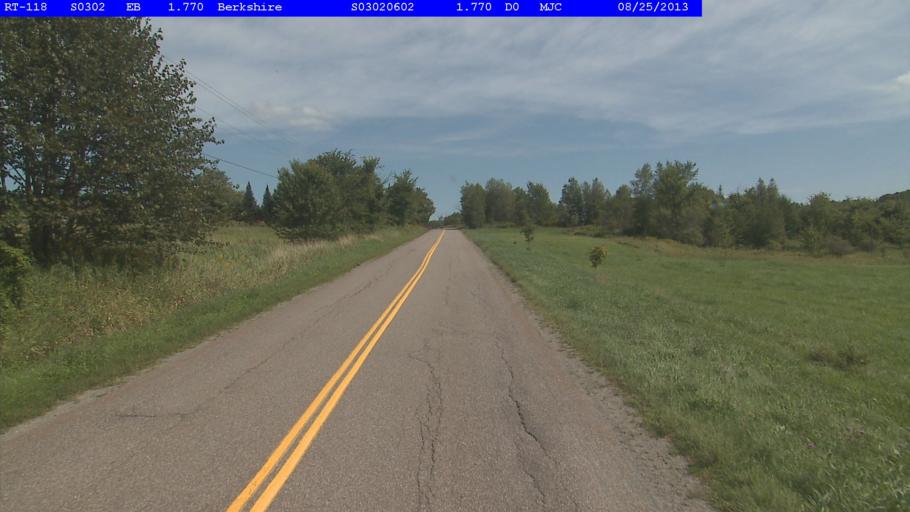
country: US
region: Vermont
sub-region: Franklin County
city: Enosburg Falls
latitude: 44.9787
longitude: -72.7817
